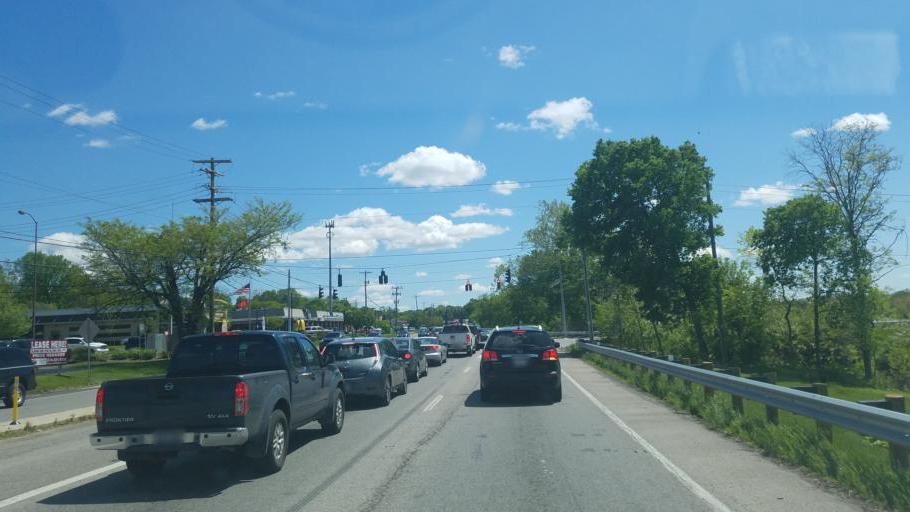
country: US
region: Ohio
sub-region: Franklin County
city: Upper Arlington
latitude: 40.0306
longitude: -83.0922
